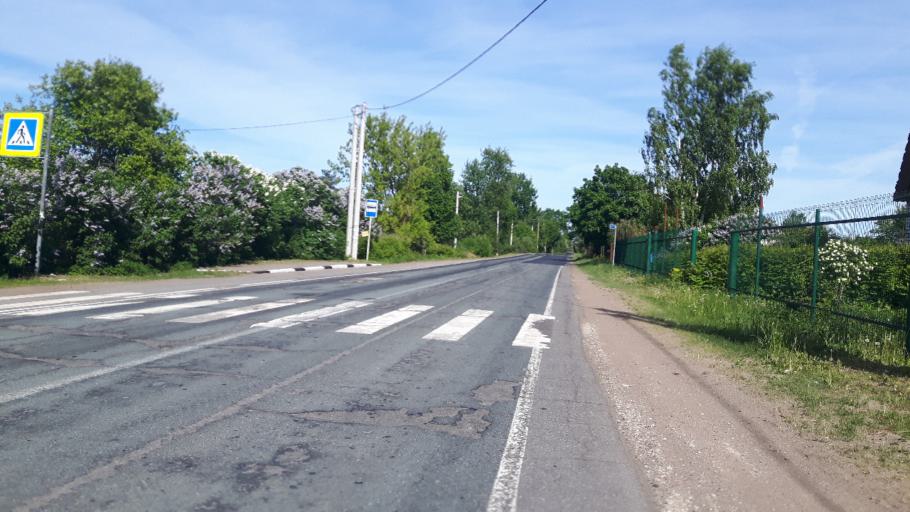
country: RU
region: Leningrad
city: Ivangorod
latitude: 59.4184
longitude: 28.3491
